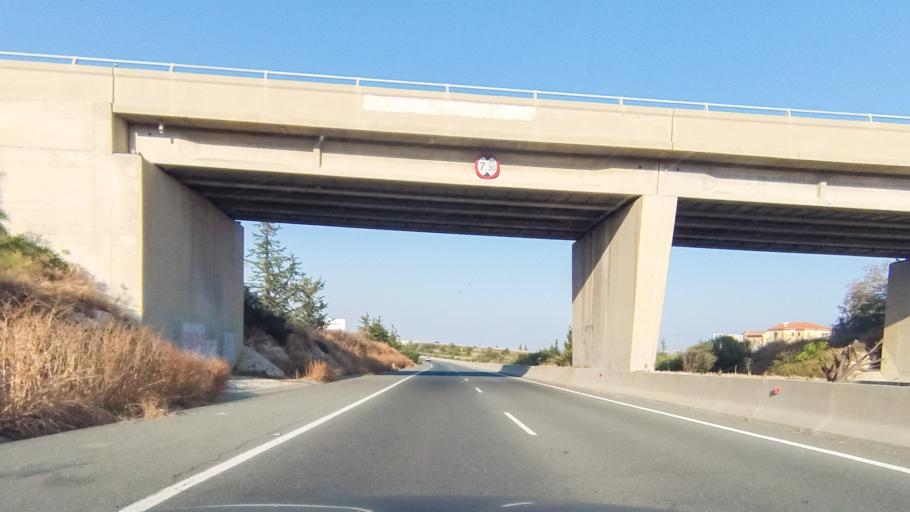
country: CY
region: Larnaka
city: Kolossi
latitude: 34.6900
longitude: 32.9365
